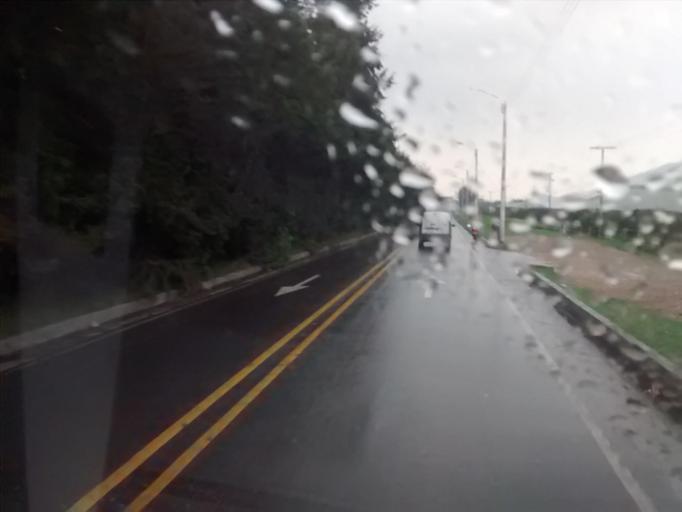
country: CO
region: Cundinamarca
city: Cota
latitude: 4.7678
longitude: -74.0857
